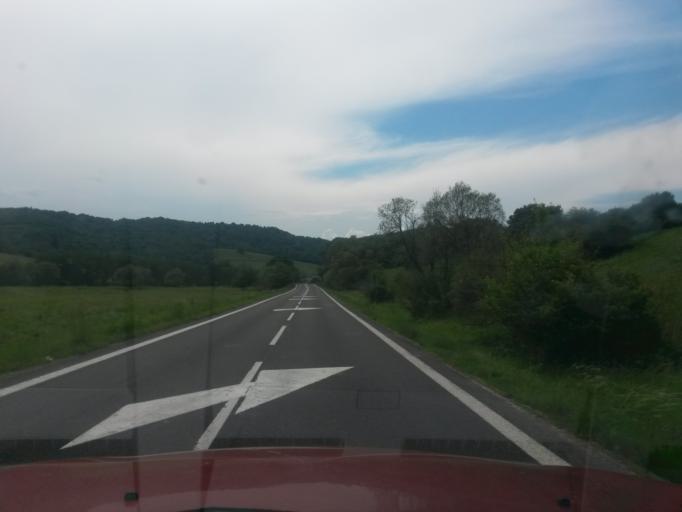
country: SK
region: Presovsky
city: Snina
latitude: 48.9885
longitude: 22.2504
